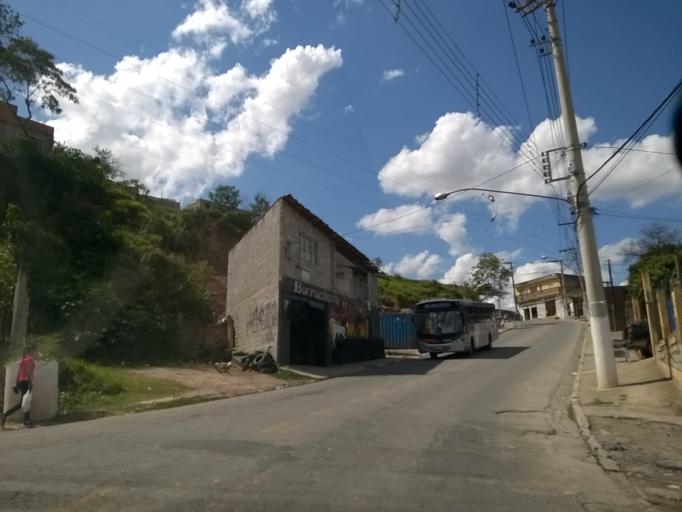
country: BR
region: Sao Paulo
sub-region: Francisco Morato
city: Francisco Morato
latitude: -23.2981
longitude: -46.7373
